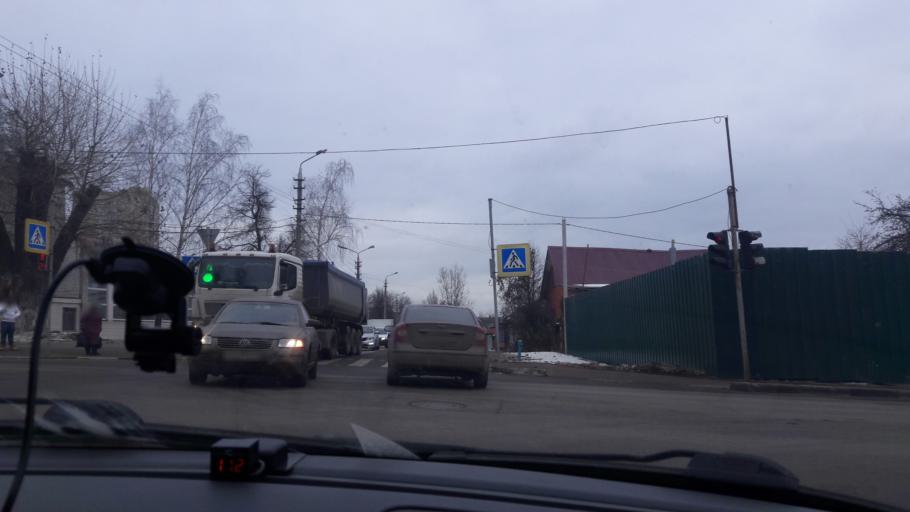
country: RU
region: Tula
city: Tula
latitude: 54.2061
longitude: 37.6538
